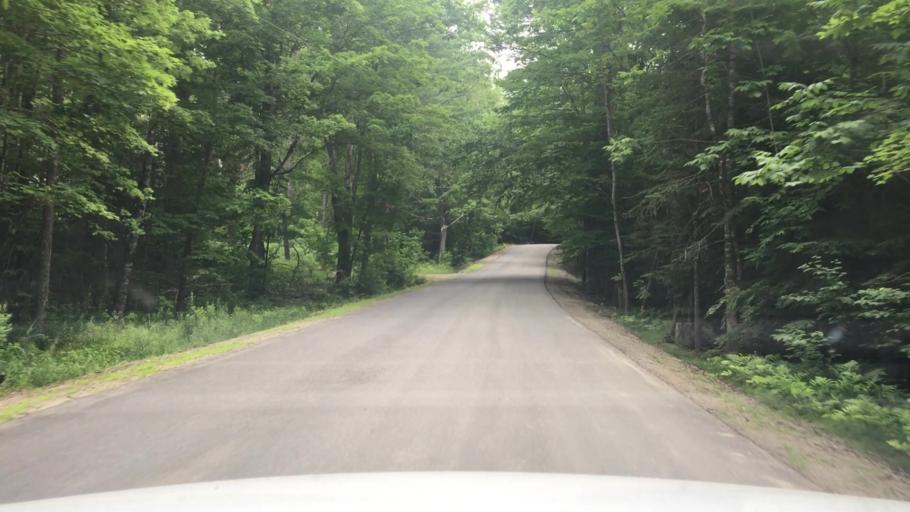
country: US
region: Maine
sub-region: Kennebec County
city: Albion
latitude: 44.4544
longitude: -69.3198
